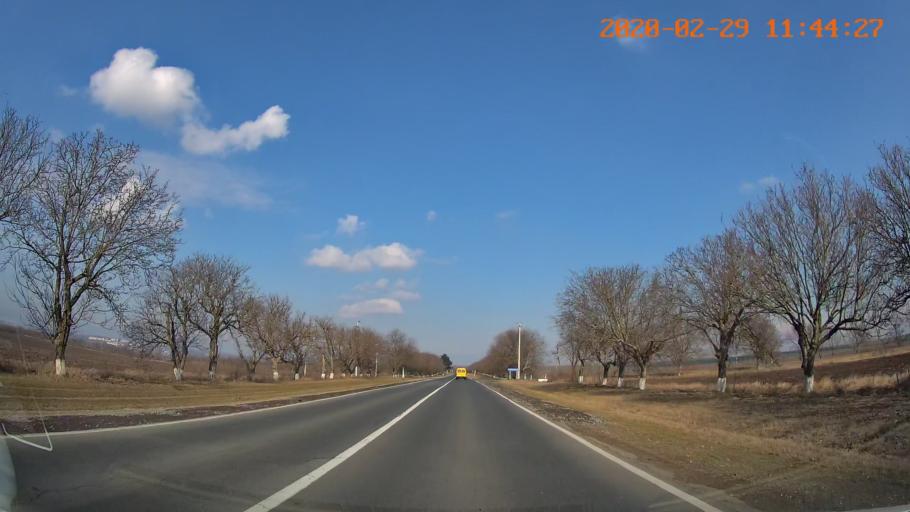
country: MD
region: Rezina
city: Saharna
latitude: 47.7116
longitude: 29.0008
